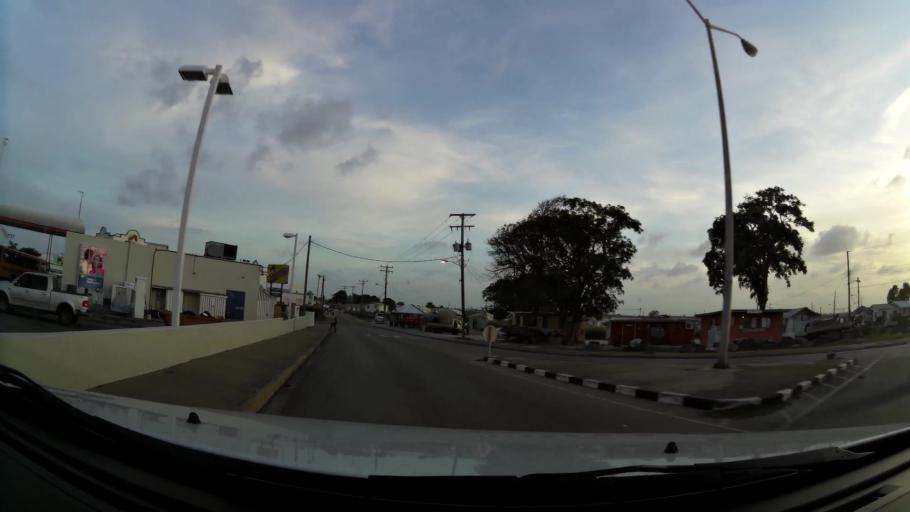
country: BB
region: Saint Philip
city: Crane
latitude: 13.1178
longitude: -59.4768
